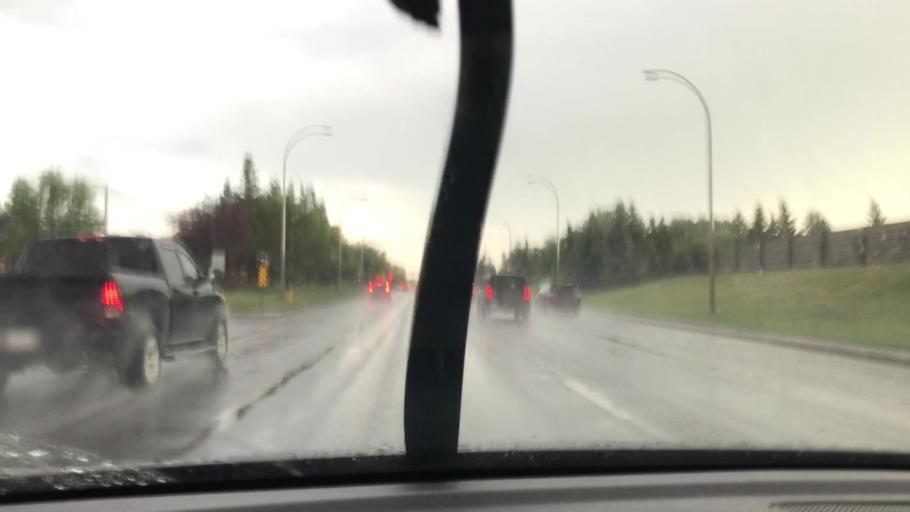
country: CA
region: Alberta
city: Edmonton
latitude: 53.4749
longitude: -113.4956
